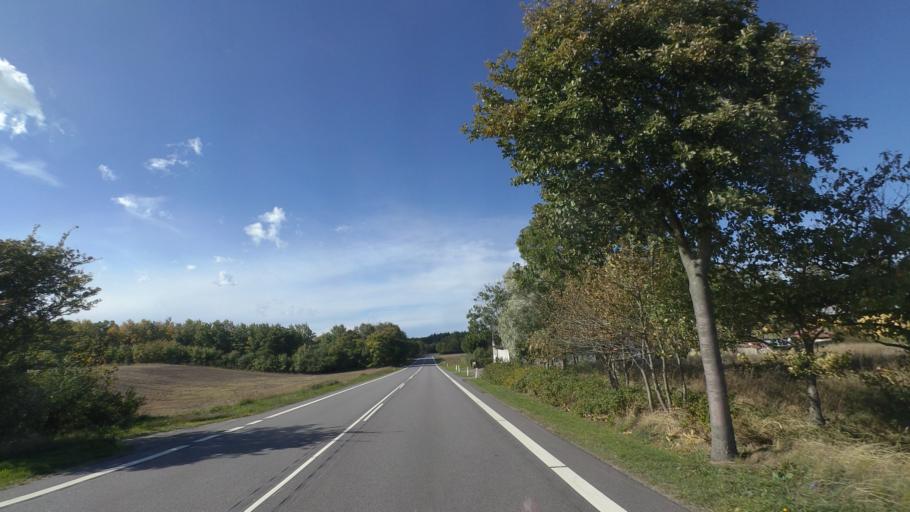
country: DK
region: Capital Region
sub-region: Bornholm Kommune
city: Ronne
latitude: 55.0789
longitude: 14.7629
